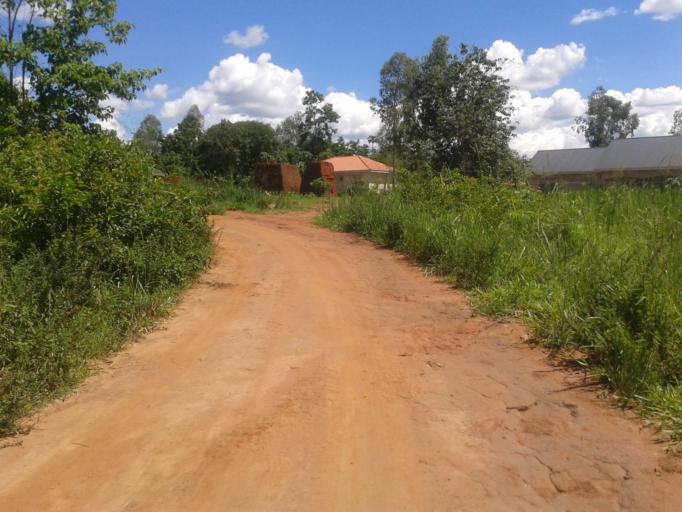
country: UG
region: Northern Region
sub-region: Gulu District
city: Gulu
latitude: 2.7626
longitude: 32.3208
